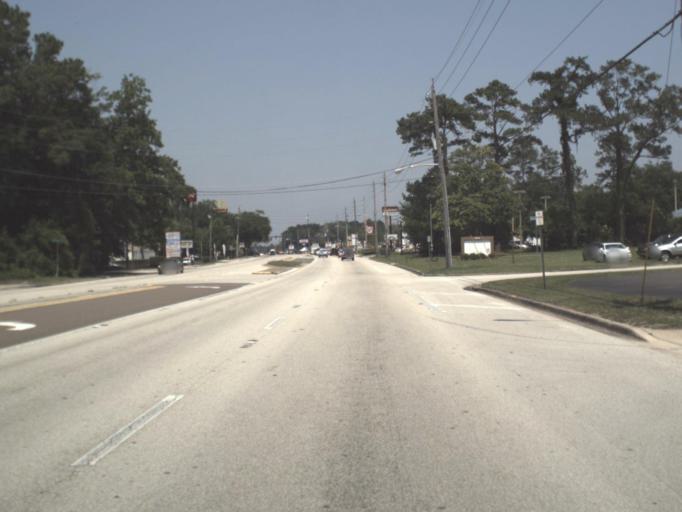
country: US
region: Florida
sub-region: Clay County
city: Bellair-Meadowbrook Terrace
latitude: 30.2912
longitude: -81.7846
